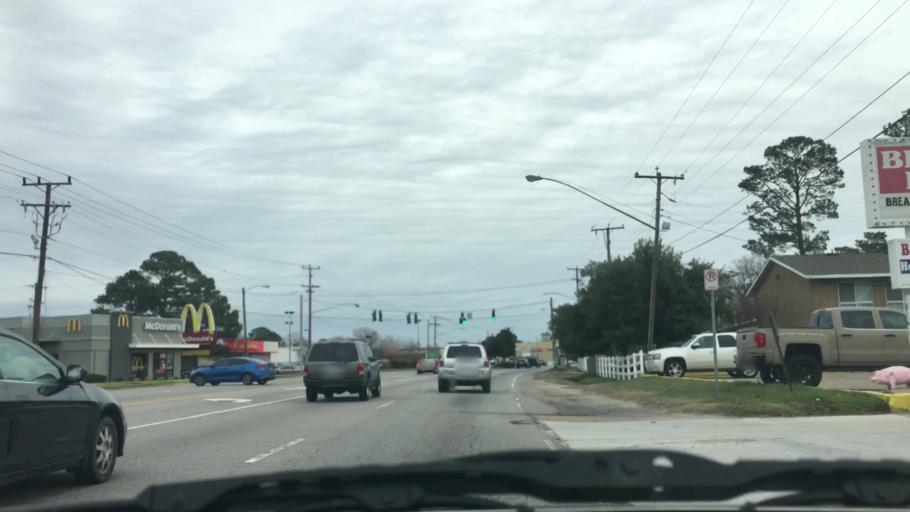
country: US
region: Virginia
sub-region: City of Norfolk
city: Norfolk
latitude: 36.9168
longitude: -76.2309
